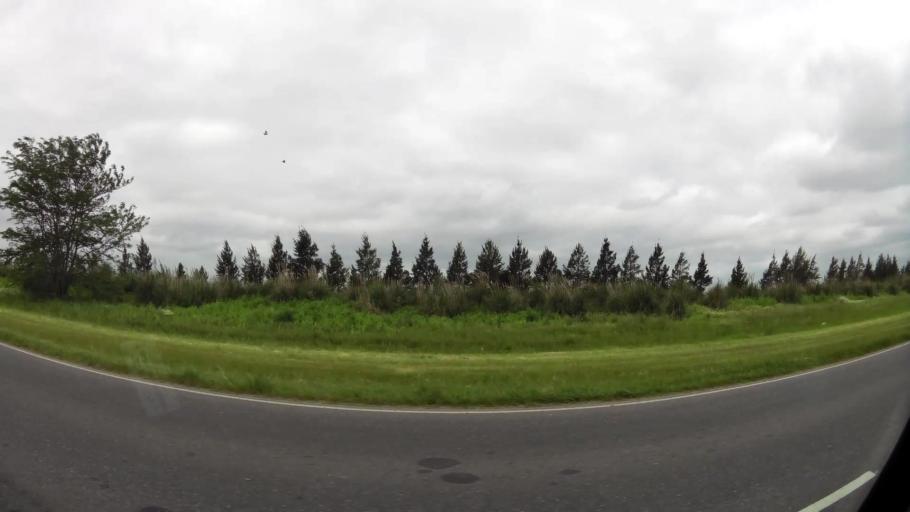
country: AR
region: Buenos Aires
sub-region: Partido de San Vicente
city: San Vicente
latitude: -35.0176
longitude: -58.4666
